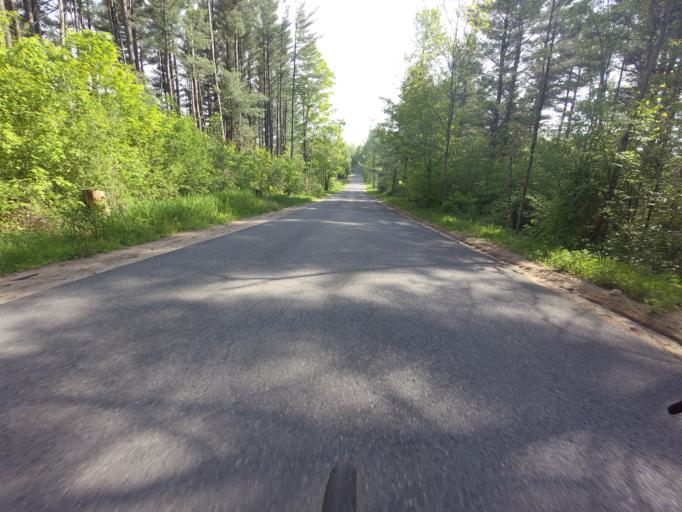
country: US
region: New York
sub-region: St. Lawrence County
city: Gouverneur
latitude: 44.2326
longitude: -75.2257
